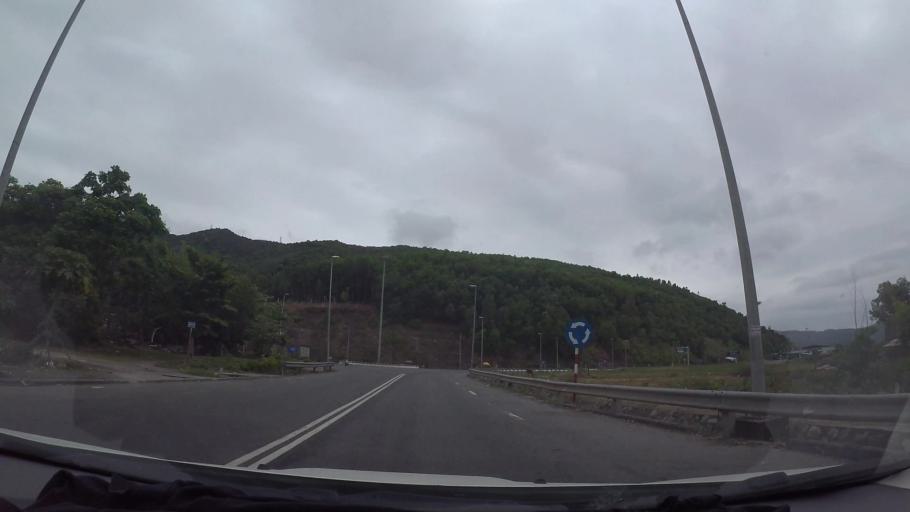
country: VN
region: Da Nang
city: Lien Chieu
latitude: 16.1306
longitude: 108.1058
